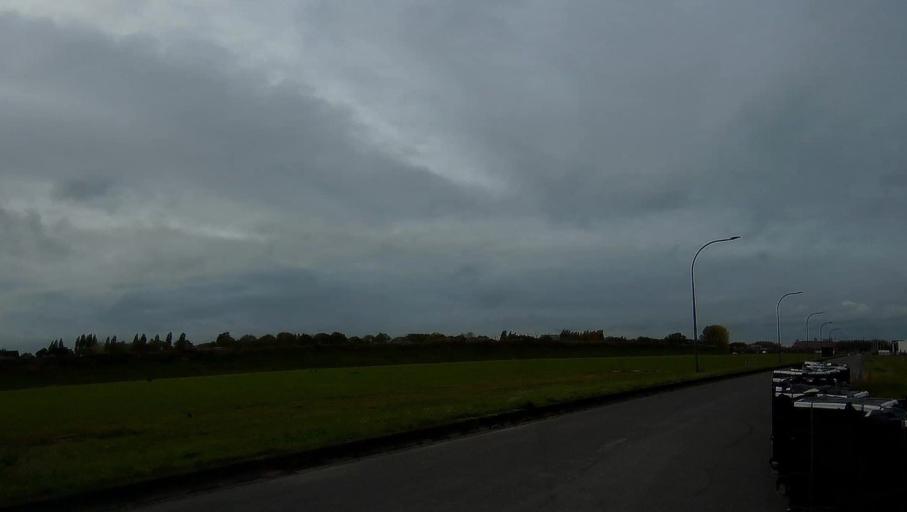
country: NL
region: South Holland
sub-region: Gemeente Zwijndrecht
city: Heerjansdam
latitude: 51.8591
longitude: 4.5722
